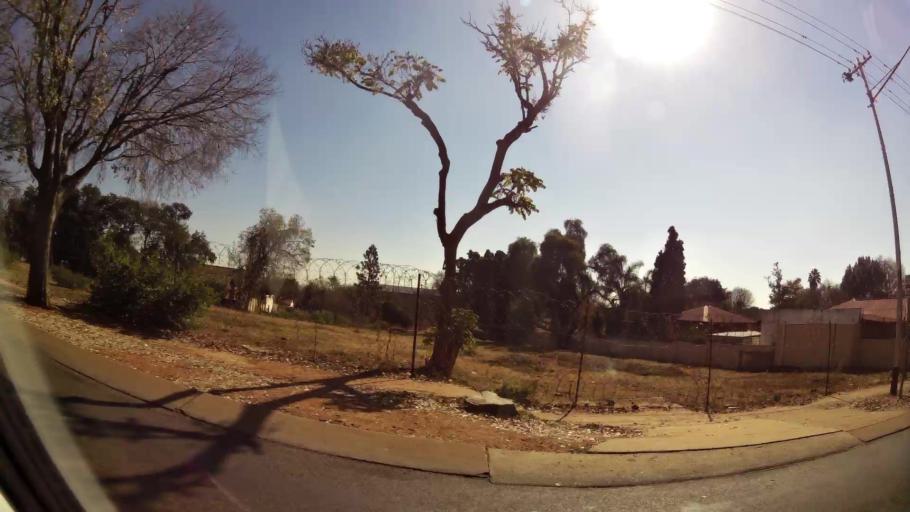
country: ZA
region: Gauteng
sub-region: City of Tshwane Metropolitan Municipality
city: Pretoria
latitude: -25.7771
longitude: 28.2266
